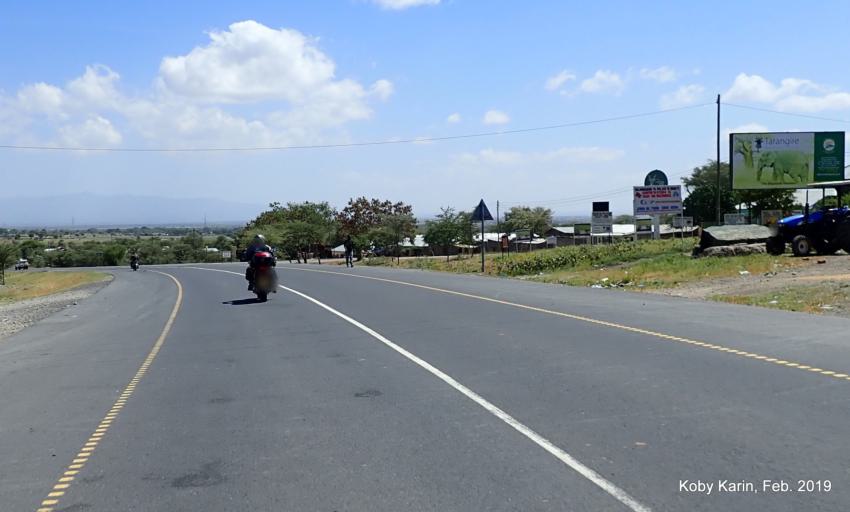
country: TZ
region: Arusha
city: Mto wa Mbu
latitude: -3.6954
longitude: 35.9365
